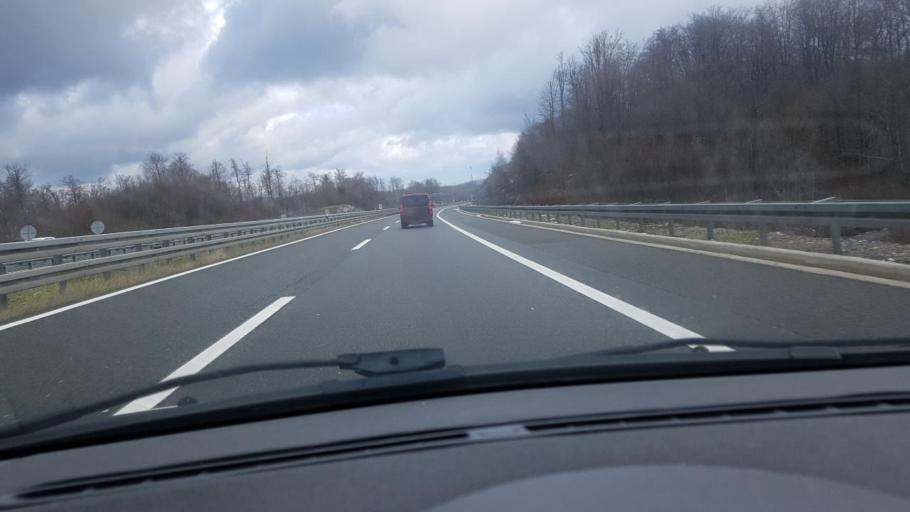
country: HR
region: Primorsko-Goranska
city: Vrbovsko
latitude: 45.3852
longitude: 15.1710
